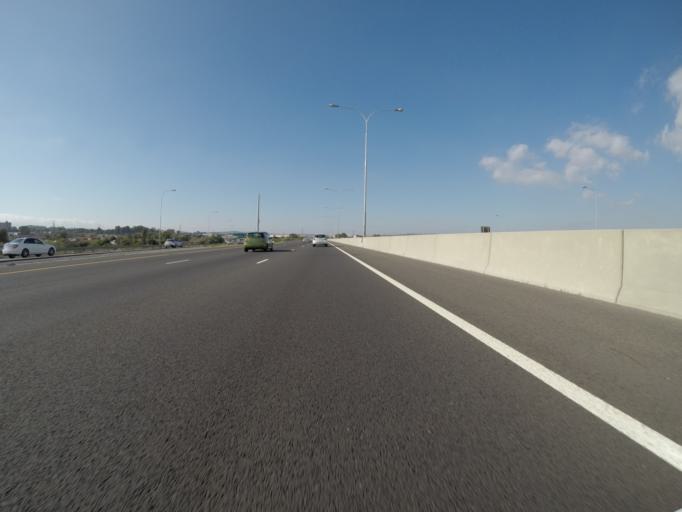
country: ZA
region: Western Cape
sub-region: City of Cape Town
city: Kraaifontein
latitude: -33.9172
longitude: 18.6668
